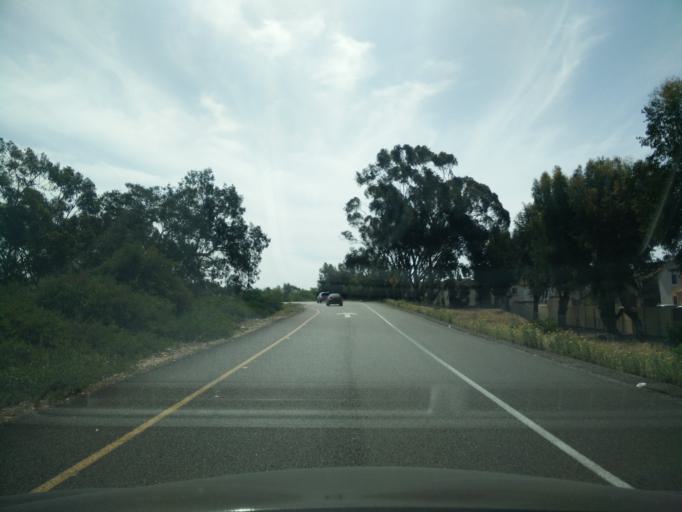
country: US
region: California
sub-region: San Diego County
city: Imperial Beach
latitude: 32.5586
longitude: -117.0639
